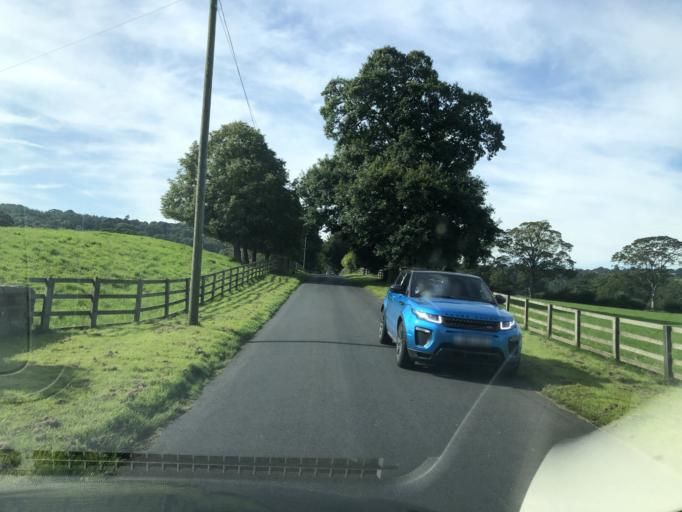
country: GB
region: England
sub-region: City and Borough of Leeds
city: Pool
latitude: 53.8969
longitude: -1.6033
